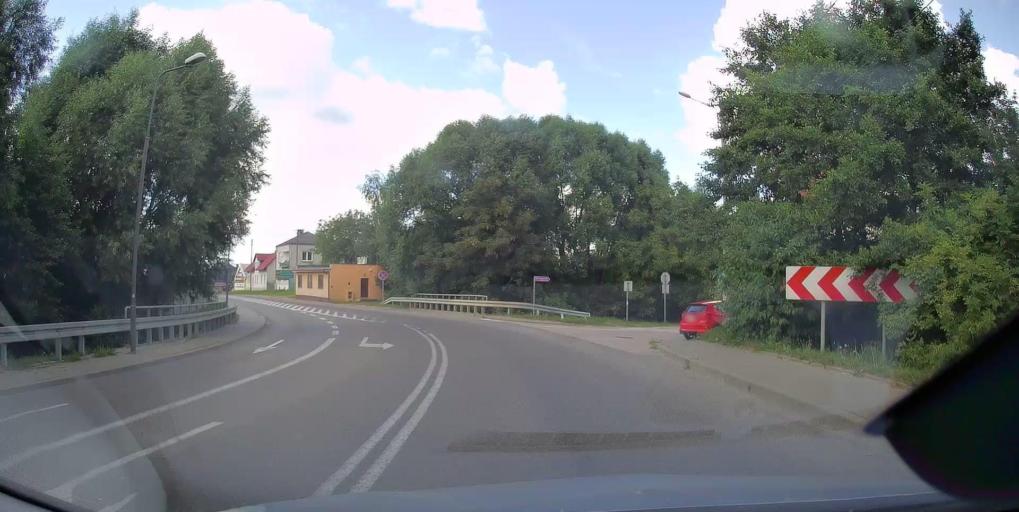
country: PL
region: Swietokrzyskie
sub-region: Powiat kielecki
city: Nowa Slupia
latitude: 50.8624
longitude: 21.0906
